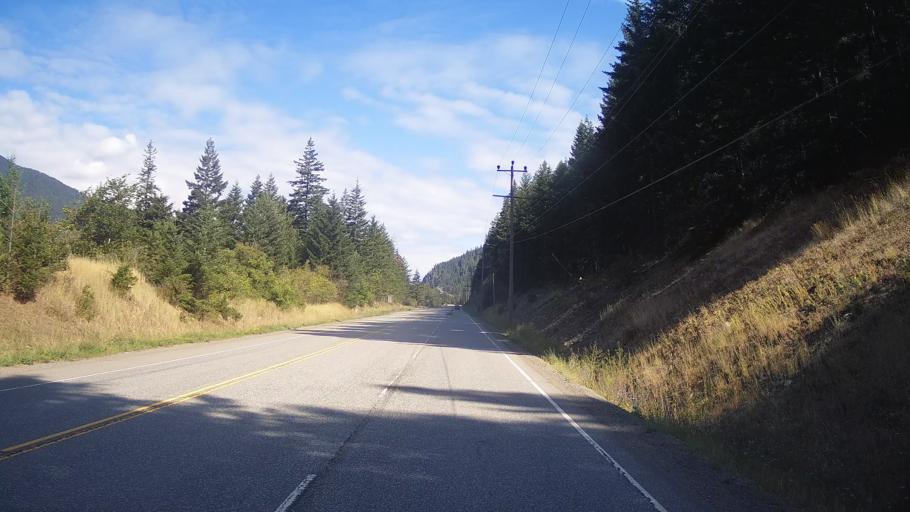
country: CA
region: British Columbia
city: Hope
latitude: 50.0561
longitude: -121.5426
